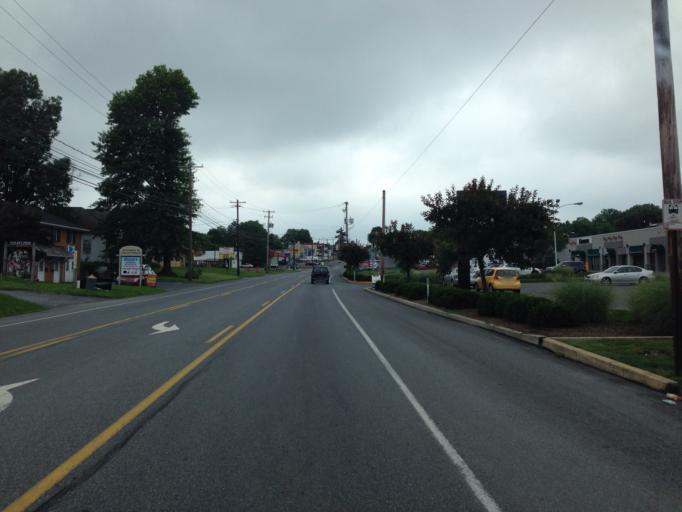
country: US
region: Pennsylvania
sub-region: Lancaster County
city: Millersville
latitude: 40.0381
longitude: -76.3517
